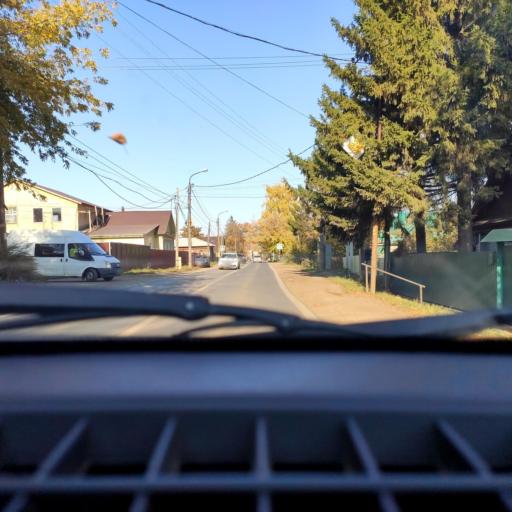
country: RU
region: Bashkortostan
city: Ufa
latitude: 54.8223
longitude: 56.1762
